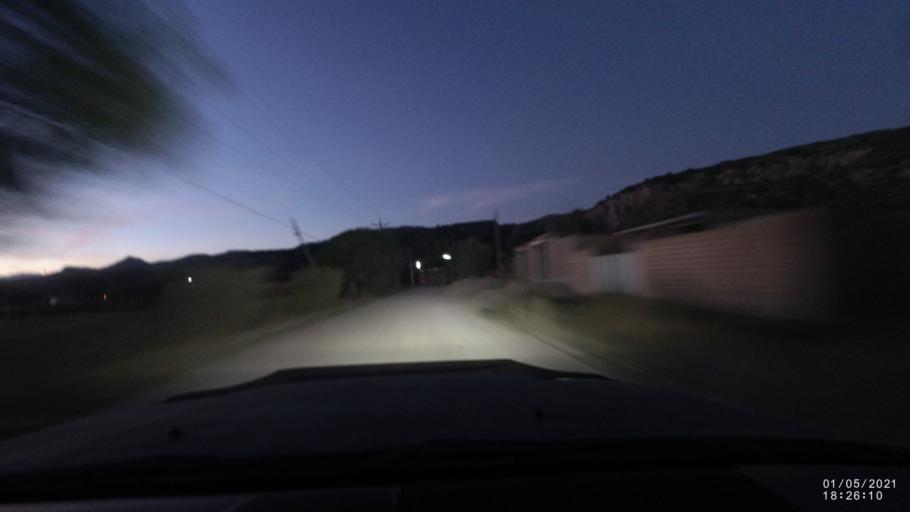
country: BO
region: Cochabamba
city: Capinota
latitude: -17.6513
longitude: -66.2410
